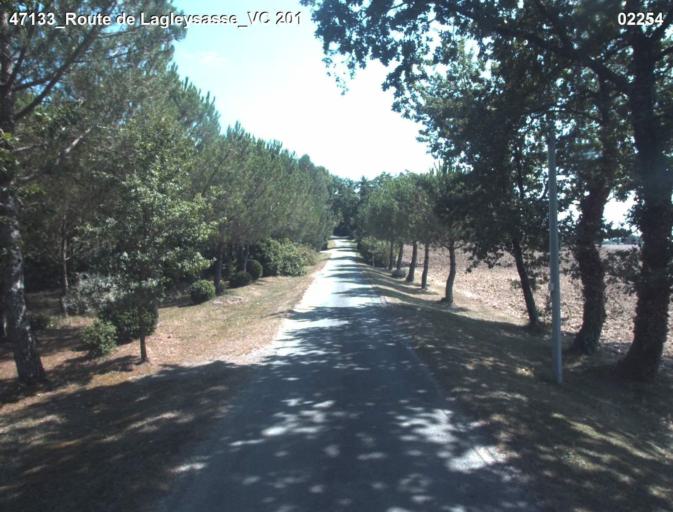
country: FR
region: Aquitaine
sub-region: Departement du Lot-et-Garonne
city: Laplume
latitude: 44.0608
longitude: 0.5325
